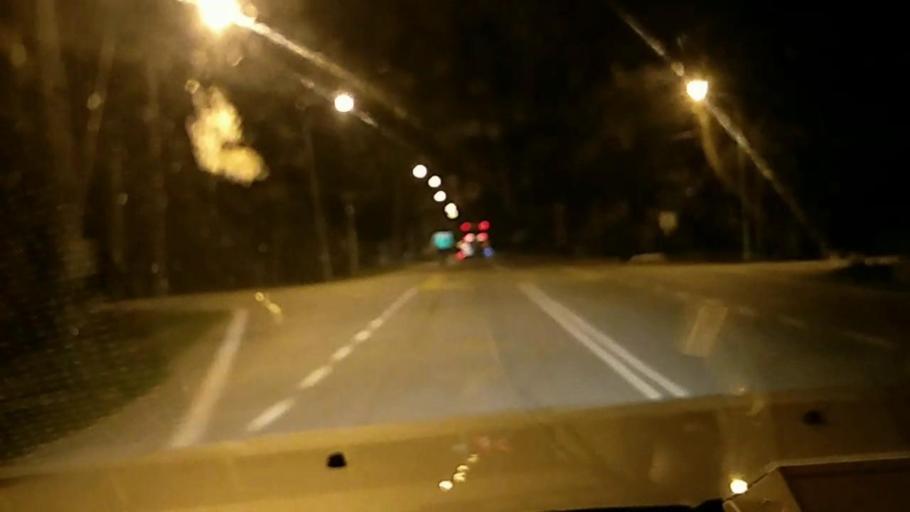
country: MY
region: Selangor
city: Kuala Selangor
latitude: 3.3028
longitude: 101.2959
